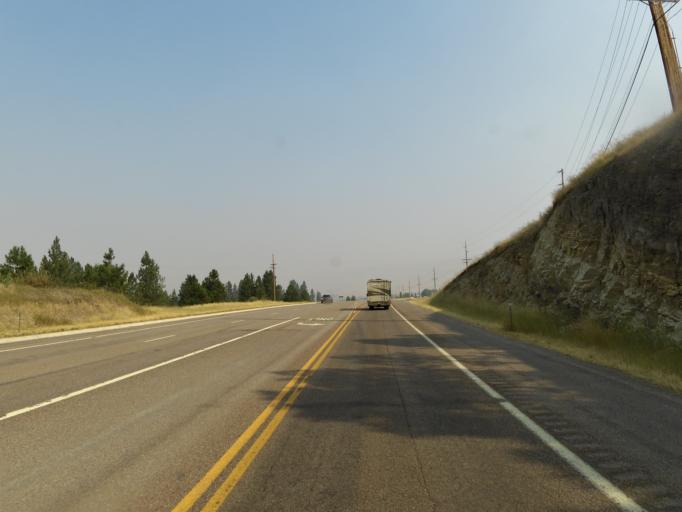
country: US
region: Montana
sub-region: Missoula County
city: Frenchtown
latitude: 47.1815
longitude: -114.1007
